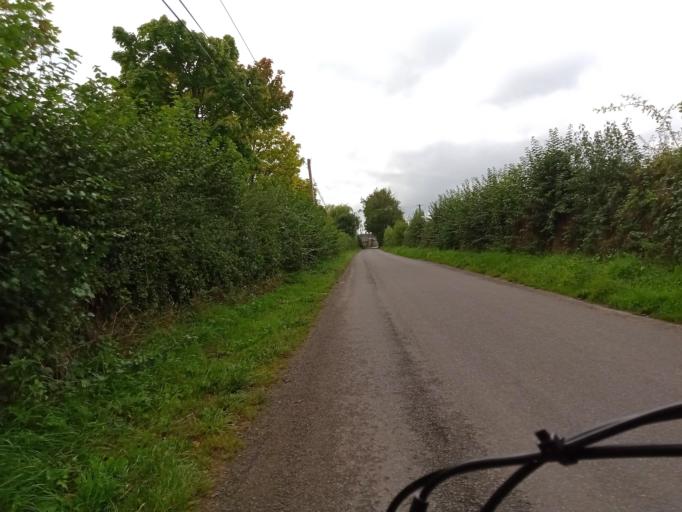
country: IE
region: Leinster
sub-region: Kilkenny
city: Callan
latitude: 52.5338
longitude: -7.2808
